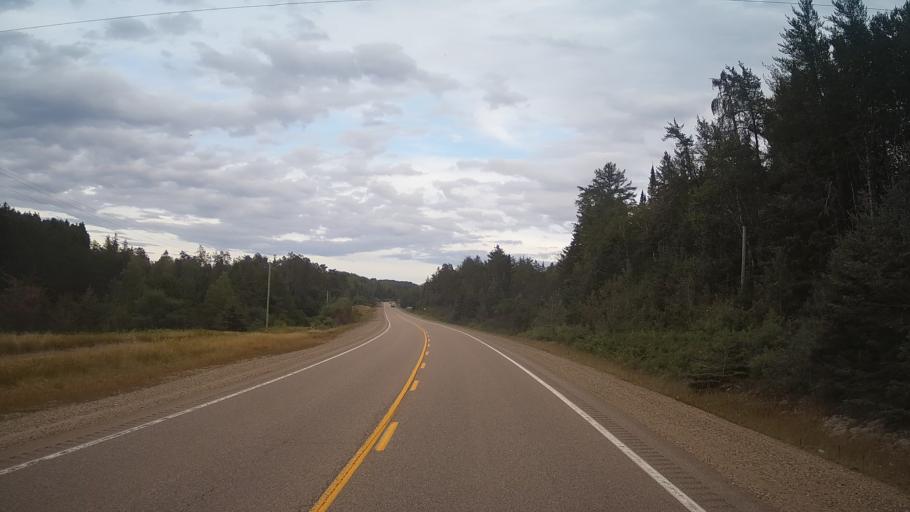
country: CA
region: Ontario
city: Deep River
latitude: 46.2123
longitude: -78.0261
